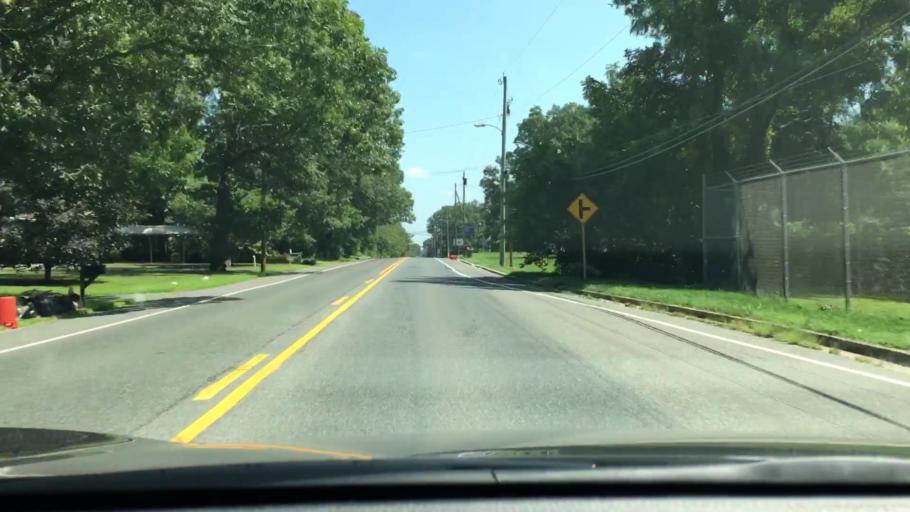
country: US
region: New Jersey
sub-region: Cumberland County
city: Millville
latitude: 39.3778
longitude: -75.0765
